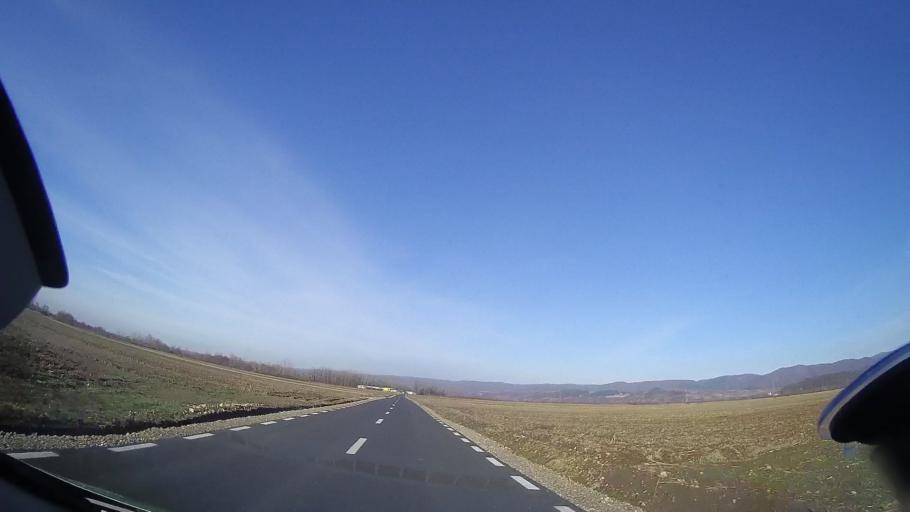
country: RO
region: Bihor
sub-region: Comuna Vadu Crisului
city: Vadu Crisului
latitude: 46.9965
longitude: 22.5061
